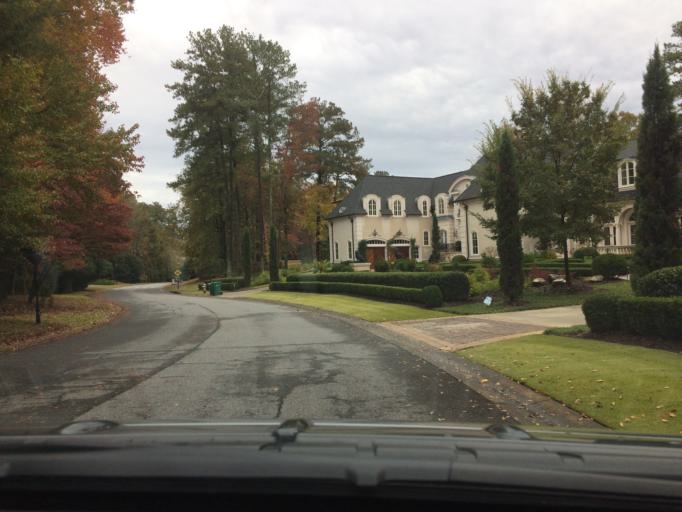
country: US
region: Georgia
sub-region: Fulton County
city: Johns Creek
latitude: 34.0108
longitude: -84.2339
